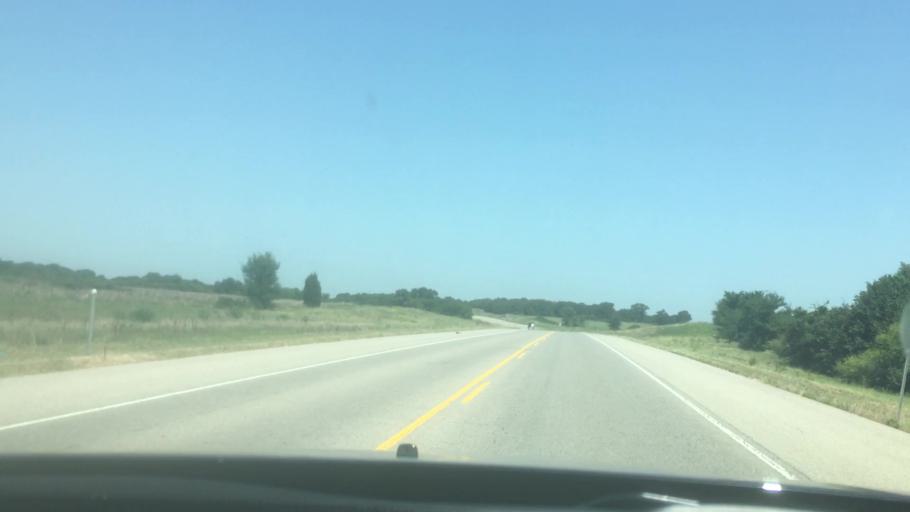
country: US
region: Oklahoma
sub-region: Pontotoc County
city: Ada
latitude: 34.6691
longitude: -96.5680
